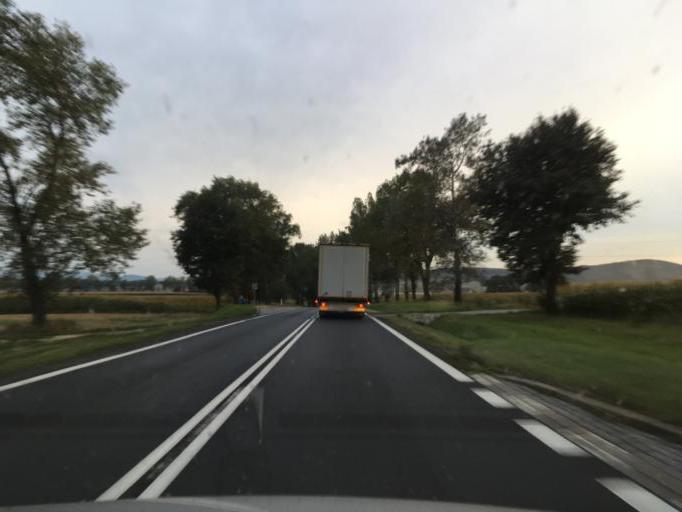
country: PL
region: Lower Silesian Voivodeship
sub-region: Powiat zabkowicki
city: Zabkowice Slaskie
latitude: 50.5736
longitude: 16.7939
